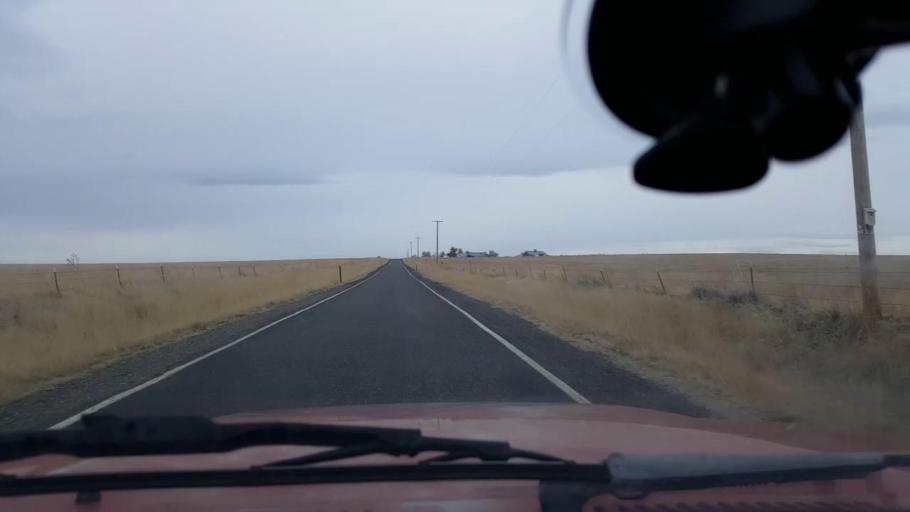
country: US
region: Washington
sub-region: Asotin County
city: Clarkston Heights-Vineland
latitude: 46.3215
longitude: -117.3272
